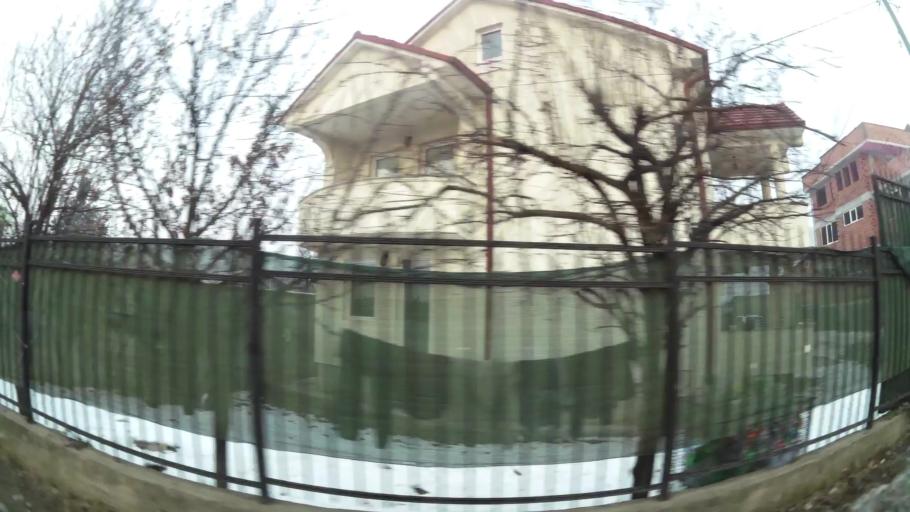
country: MK
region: Suto Orizari
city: Suto Orizare
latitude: 42.0353
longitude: 21.4143
